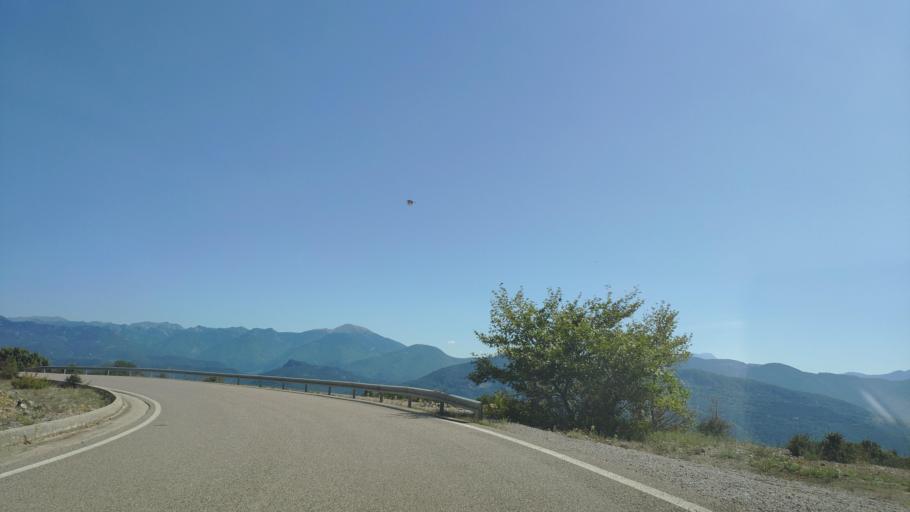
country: GR
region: Central Greece
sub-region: Nomos Evrytanias
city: Kerasochori
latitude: 38.9477
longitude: 21.4631
